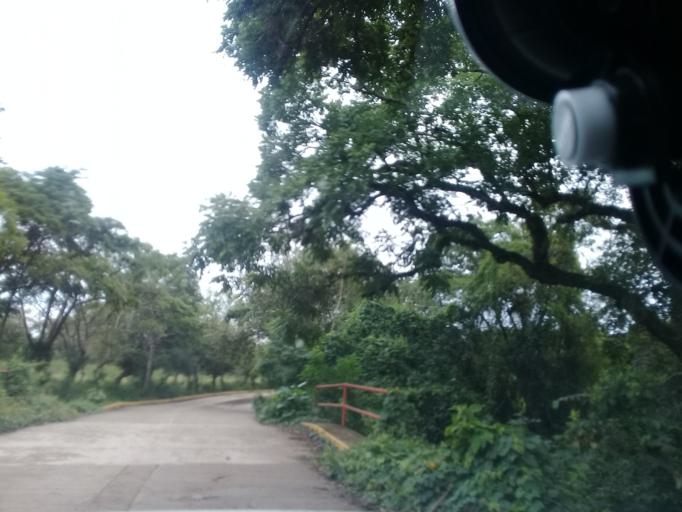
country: MX
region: Hidalgo
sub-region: Huejutla de Reyes
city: Chalahuiyapa
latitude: 21.1626
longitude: -98.3591
